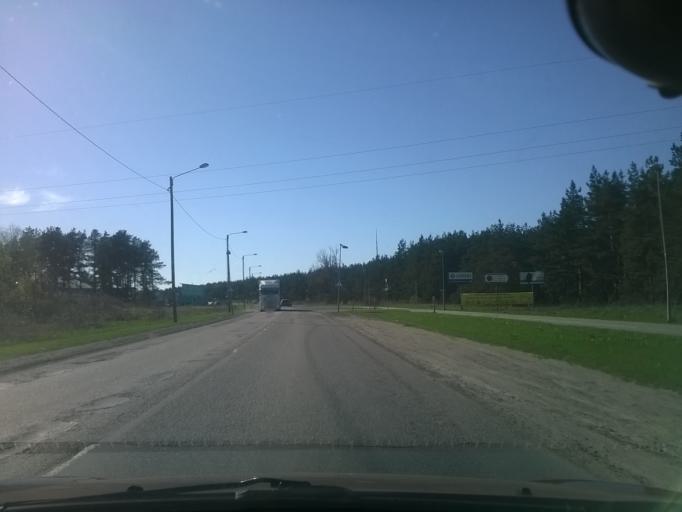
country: EE
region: Harju
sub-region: Joelaehtme vald
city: Loo
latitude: 59.4606
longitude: 24.9251
